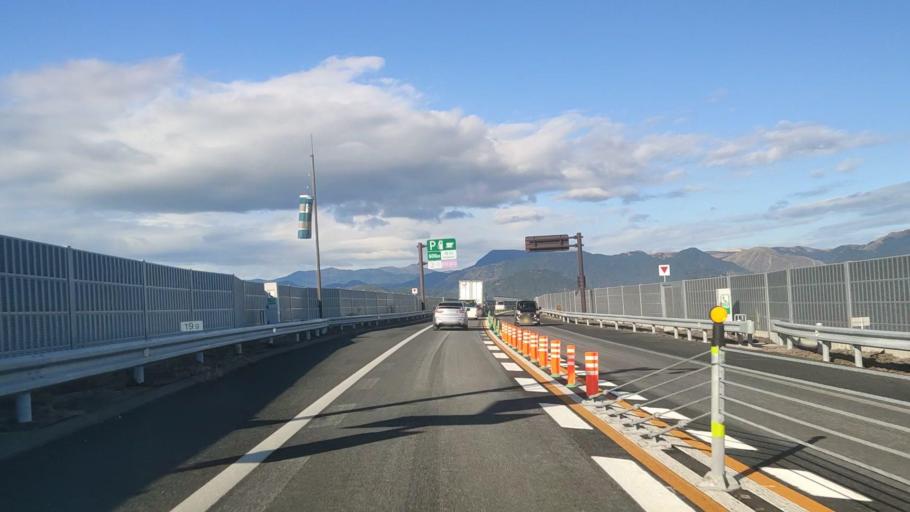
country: JP
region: Fukuoka
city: Yukuhashi
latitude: 33.7004
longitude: 130.9666
